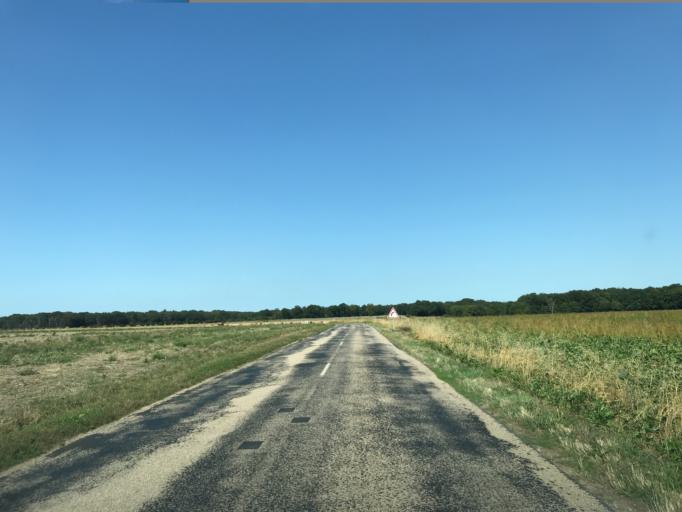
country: FR
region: Haute-Normandie
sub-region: Departement de l'Eure
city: Heudreville-sur-Eure
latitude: 49.0985
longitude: 1.2039
